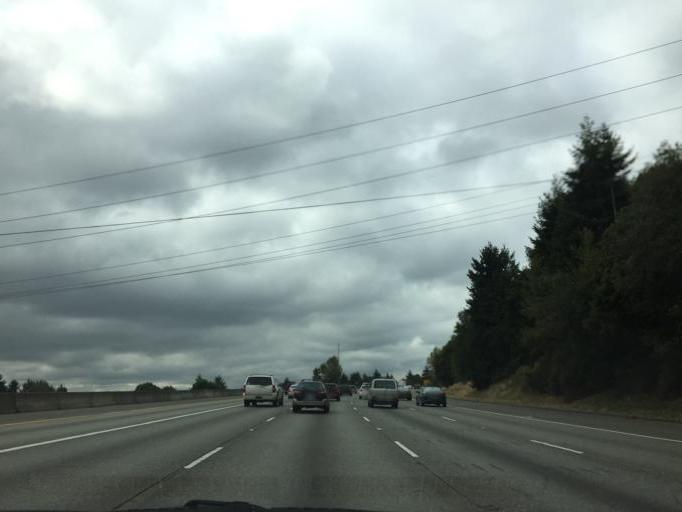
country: US
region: Washington
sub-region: King County
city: SeaTac
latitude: 47.4337
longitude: -122.2704
